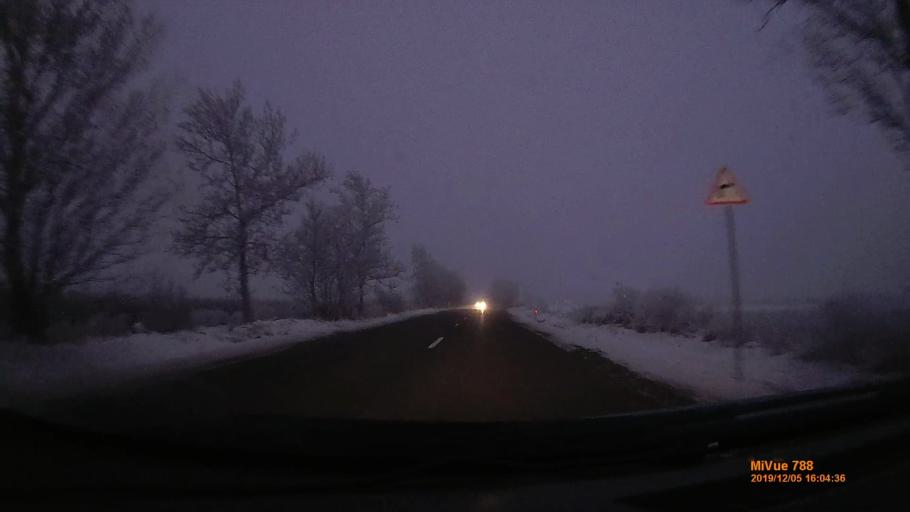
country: HU
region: Borsod-Abauj-Zemplen
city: Tarcal
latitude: 48.1092
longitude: 21.3532
